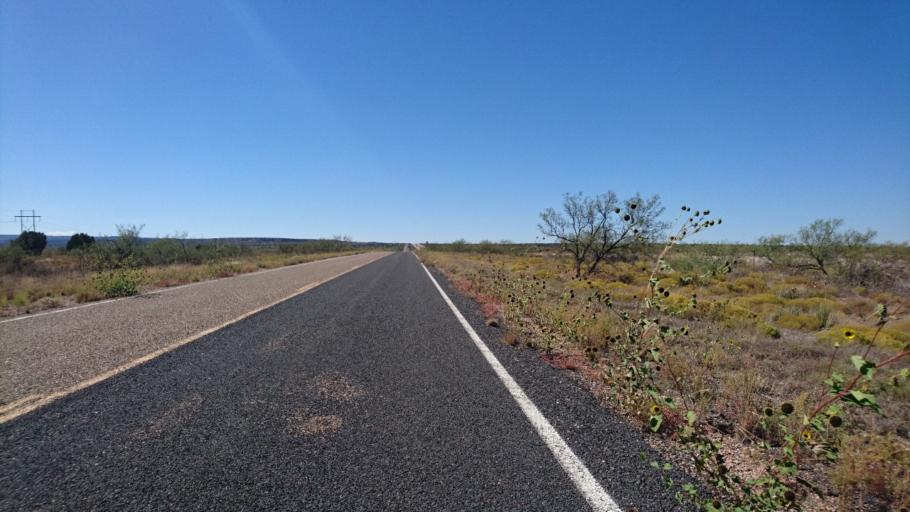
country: US
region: New Mexico
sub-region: Quay County
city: Tucumcari
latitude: 35.0776
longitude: -104.1326
